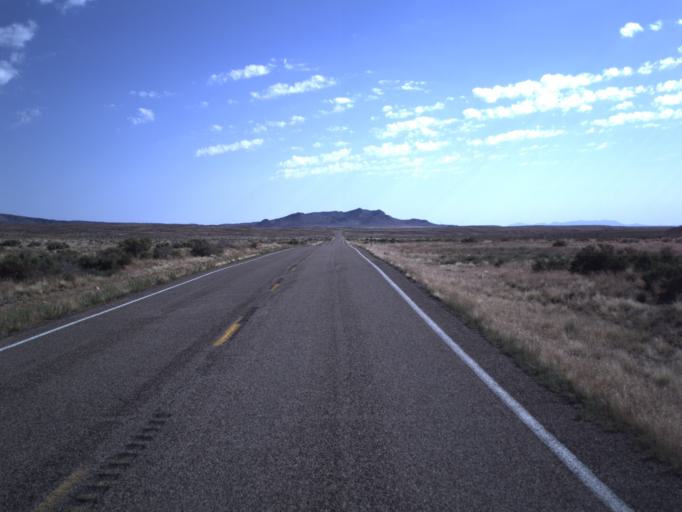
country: US
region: Utah
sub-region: Beaver County
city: Milford
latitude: 38.7494
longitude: -112.9503
